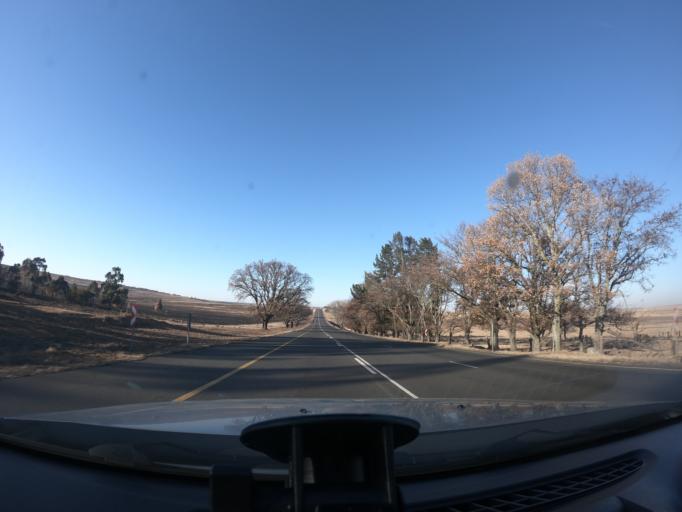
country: ZA
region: Mpumalanga
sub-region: Gert Sibande District Municipality
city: Ermelo
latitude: -26.4477
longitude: 29.9489
